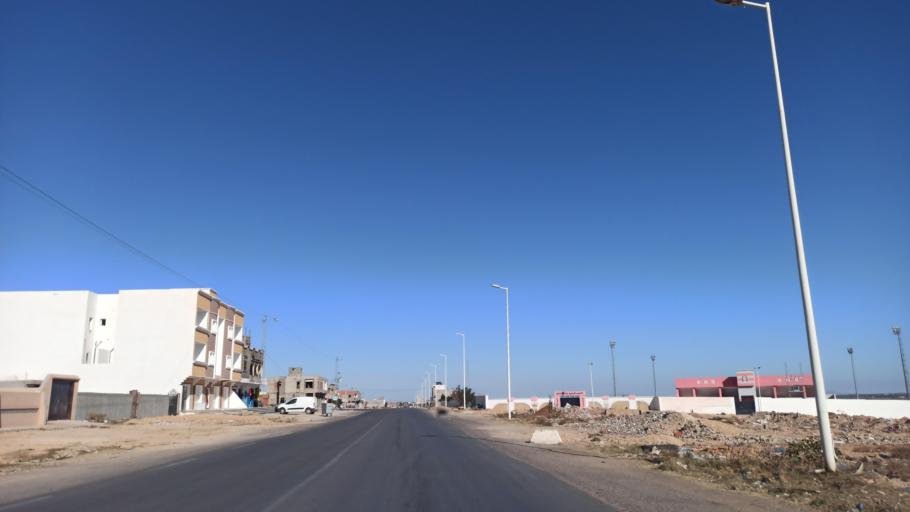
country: TN
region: Sidi Bu Zayd
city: Bi'r al Hufayy
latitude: 34.9414
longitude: 9.2037
